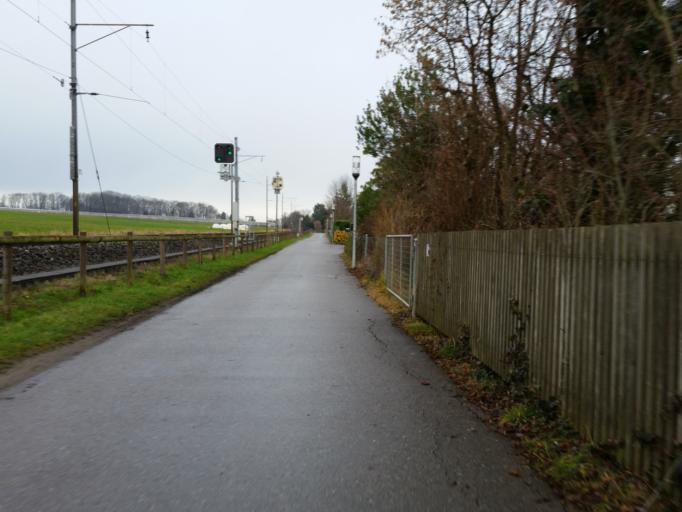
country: CH
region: Thurgau
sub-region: Arbon District
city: Romanshorn
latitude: 47.5758
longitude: 9.3681
